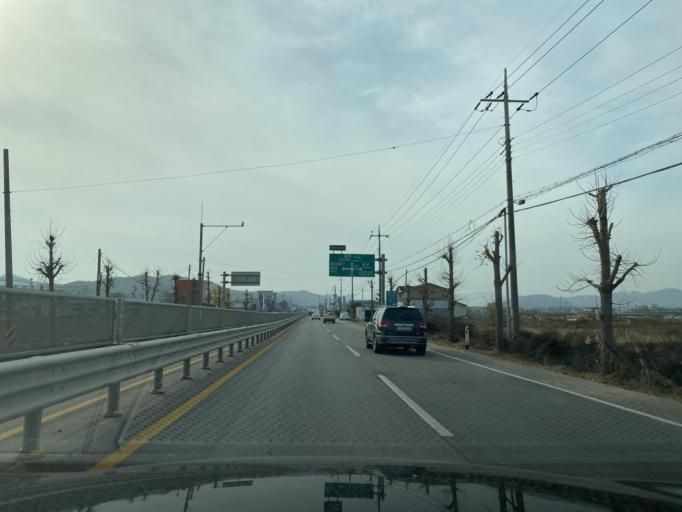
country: KR
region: Chungcheongnam-do
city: Yesan
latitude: 36.6882
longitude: 126.8273
